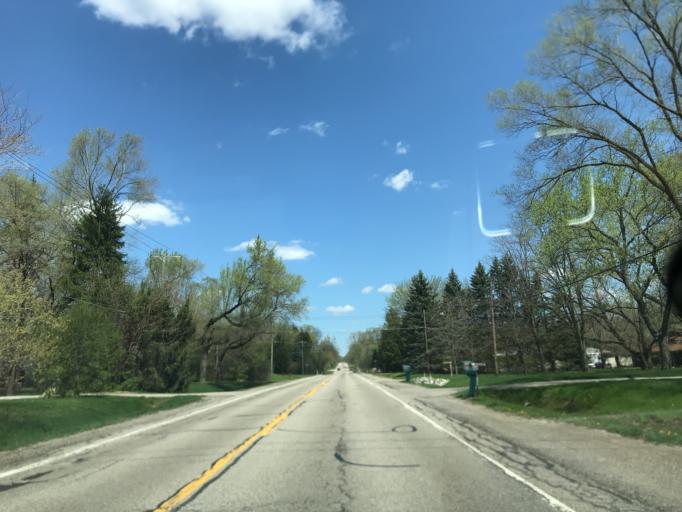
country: US
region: Michigan
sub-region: Oakland County
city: Farmington
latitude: 42.4710
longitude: -83.3670
